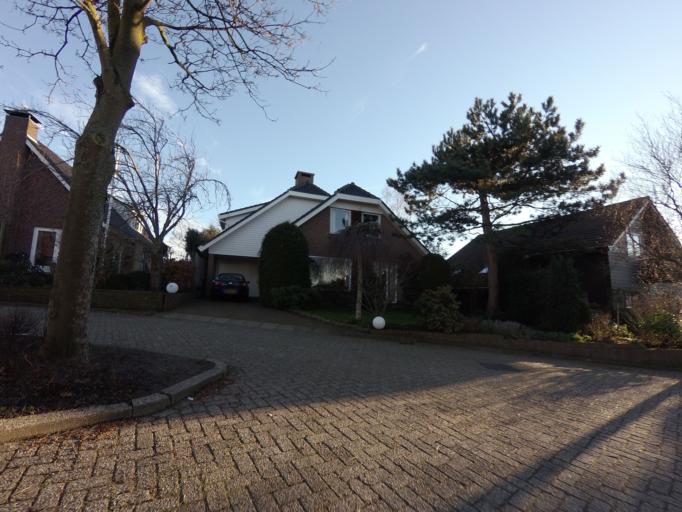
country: NL
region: South Holland
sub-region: Gemeente Alphen aan den Rijn
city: Alphen aan den Rijn
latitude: 52.1694
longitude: 4.6369
